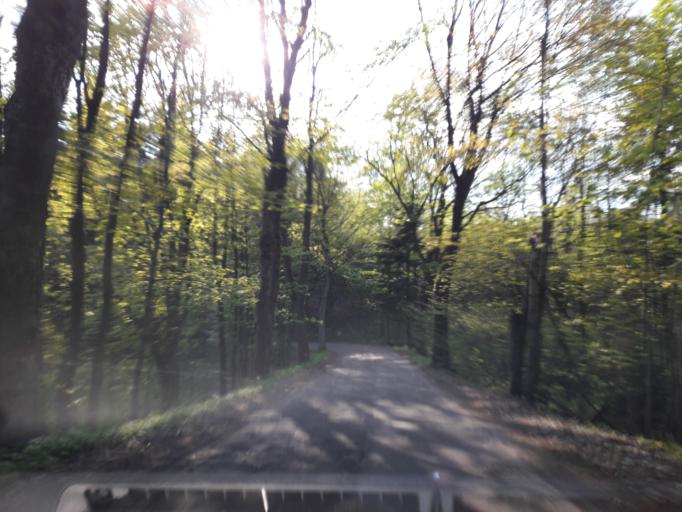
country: PL
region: Lower Silesian Voivodeship
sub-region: Powiat klodzki
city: Duszniki-Zdroj
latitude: 50.4458
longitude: 16.3490
